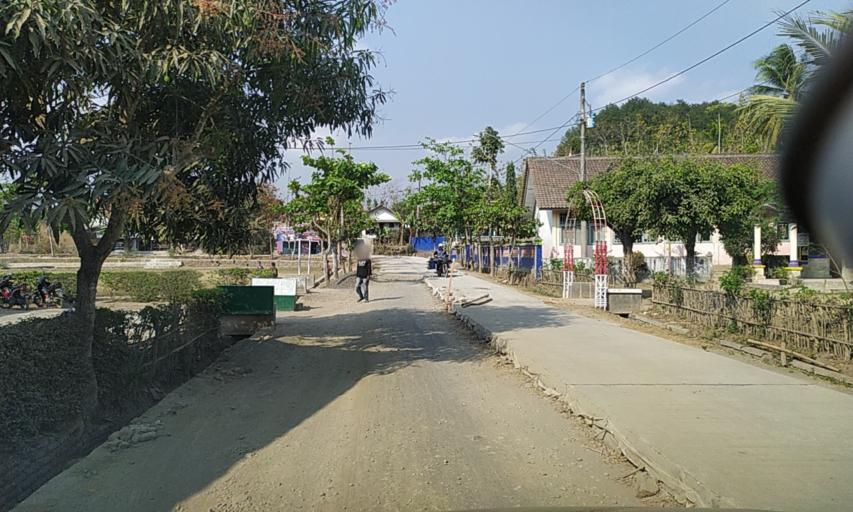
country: ID
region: Central Java
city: Muktisari
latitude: -7.4967
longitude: 108.8974
